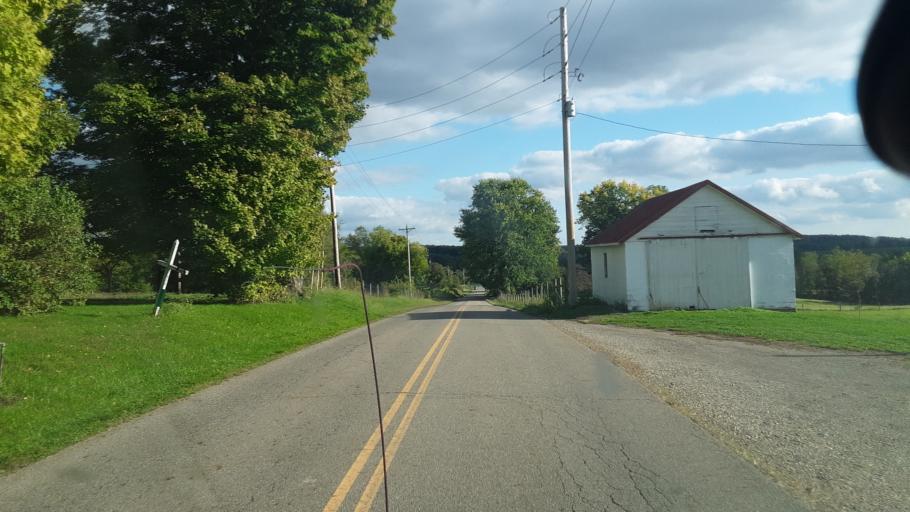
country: US
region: Ohio
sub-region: Knox County
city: Fredericktown
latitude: 40.4911
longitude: -82.4858
